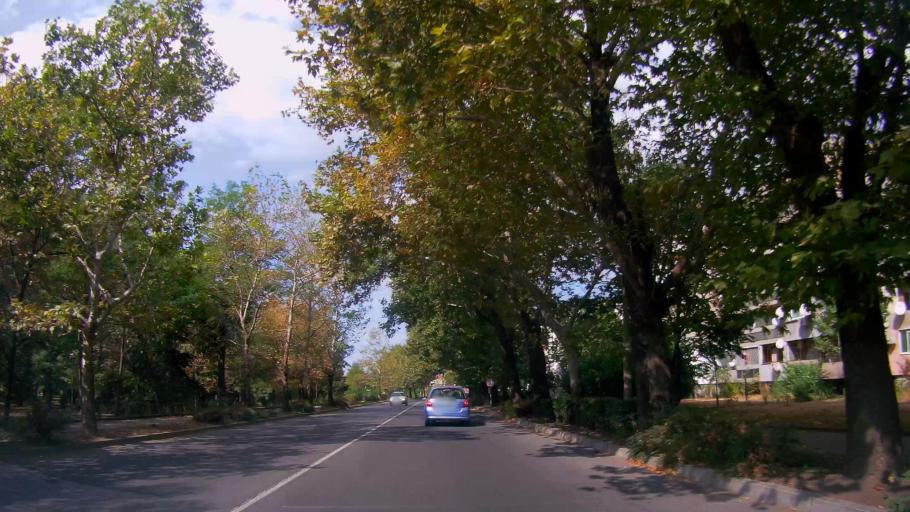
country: BG
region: Burgas
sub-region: Obshtina Aytos
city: Aytos
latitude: 42.6985
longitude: 27.2512
